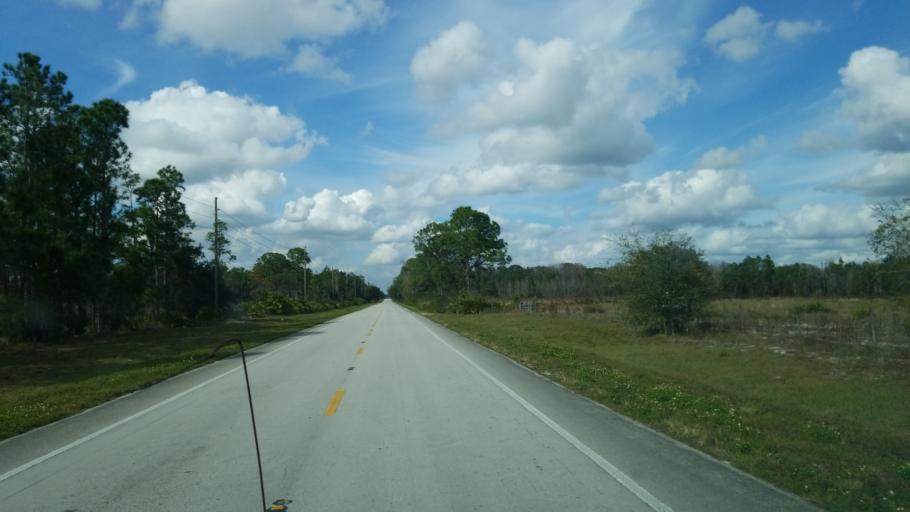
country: US
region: Florida
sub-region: Brevard County
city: June Park
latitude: 27.9736
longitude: -81.0091
